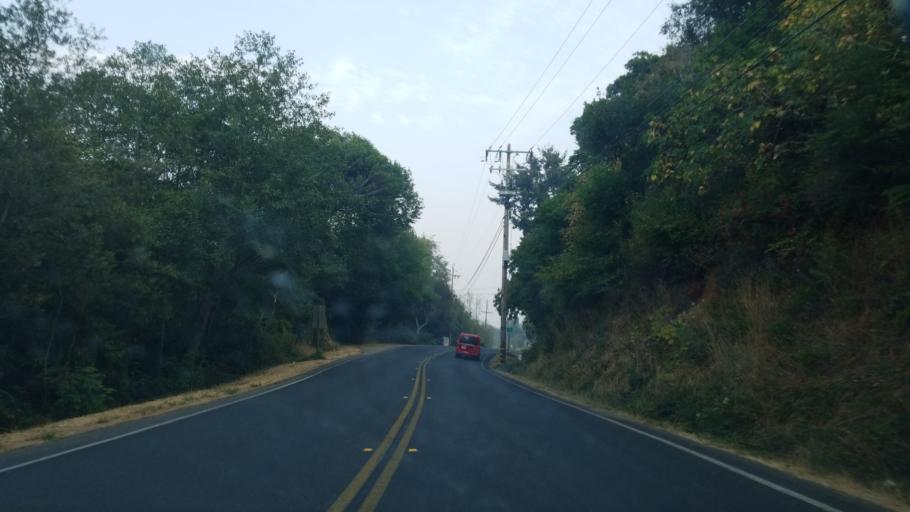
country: US
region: California
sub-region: Marin County
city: Inverness
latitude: 38.0775
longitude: -122.8320
